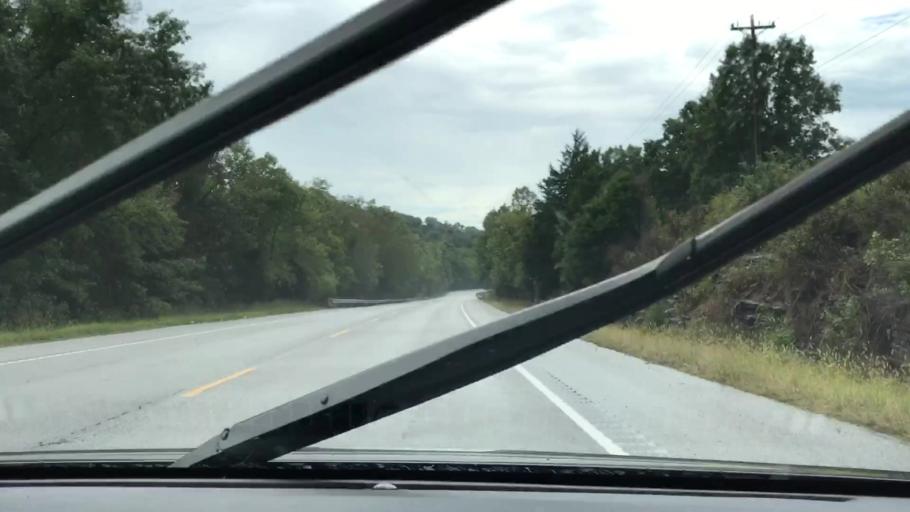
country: US
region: Tennessee
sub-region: Smith County
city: Carthage
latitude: 36.2948
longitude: -85.9829
